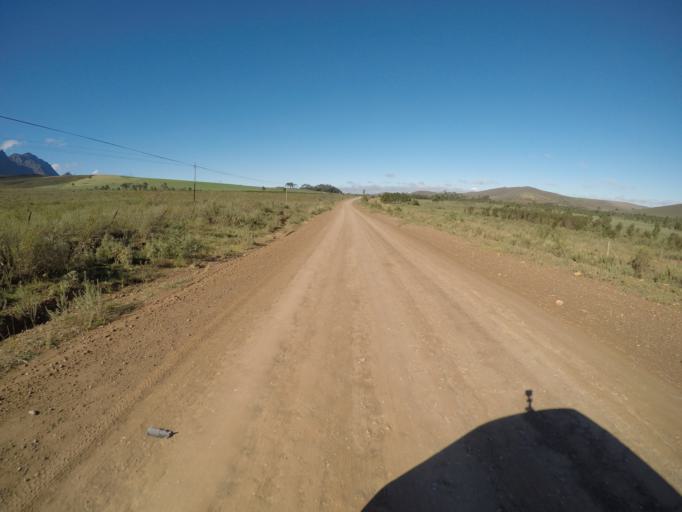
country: ZA
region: Western Cape
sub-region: Overberg District Municipality
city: Caledon
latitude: -34.0634
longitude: 19.6260
